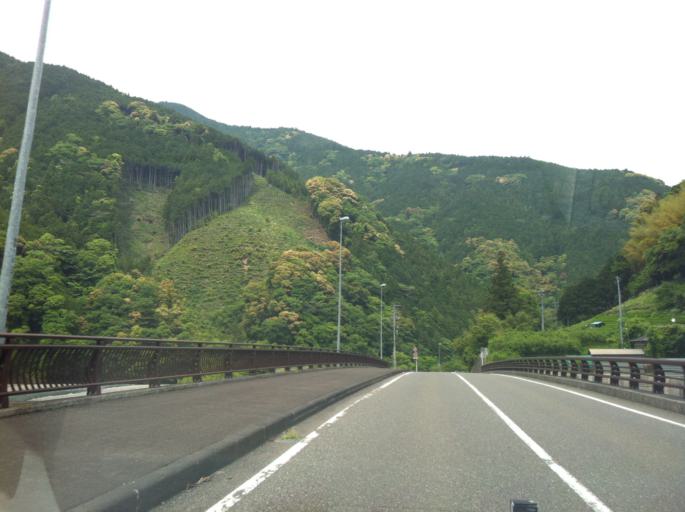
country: JP
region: Shizuoka
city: Shizuoka-shi
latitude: 35.1127
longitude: 138.3451
